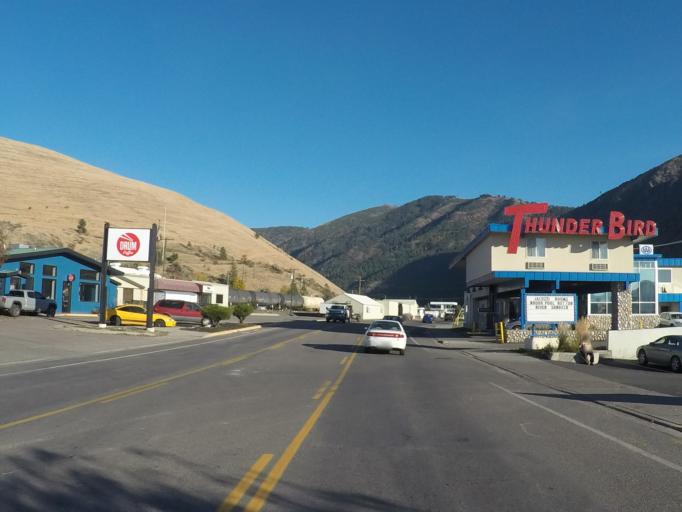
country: US
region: Montana
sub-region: Missoula County
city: Missoula
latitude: 46.8681
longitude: -113.9808
